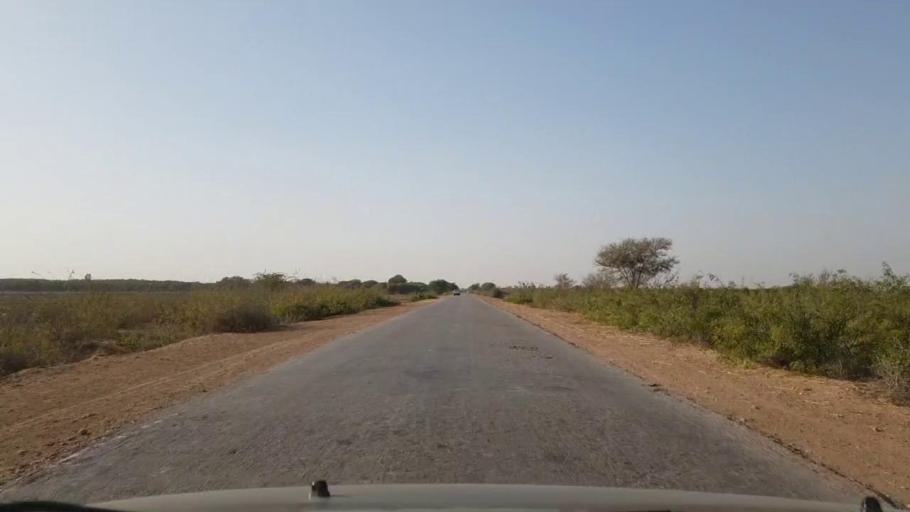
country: PK
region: Sindh
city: Tando Ghulam Ali
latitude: 25.1882
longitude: 68.8121
